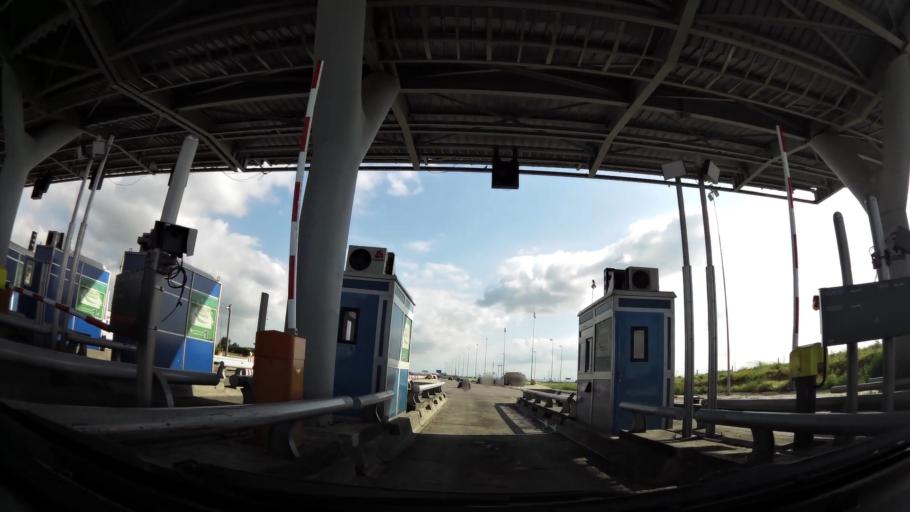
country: MA
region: Chaouia-Ouardigha
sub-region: Settat Province
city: Berrechid
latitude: 33.2323
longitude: -7.5727
